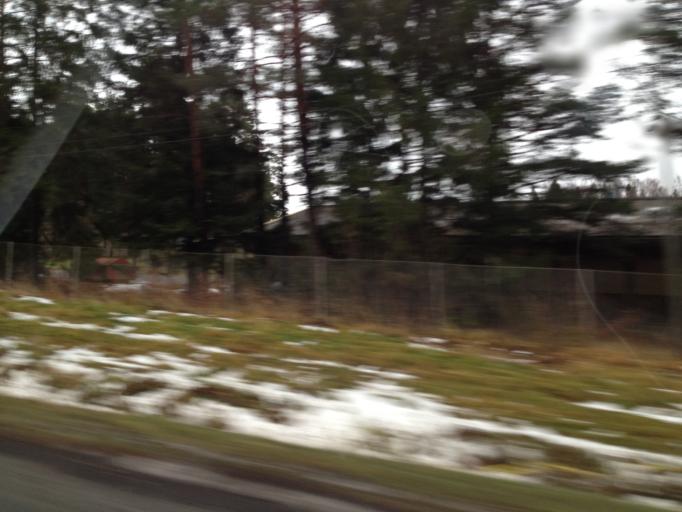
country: FI
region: Uusimaa
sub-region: Raaseporin
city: Ekenaes
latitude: 59.9724
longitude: 23.3894
